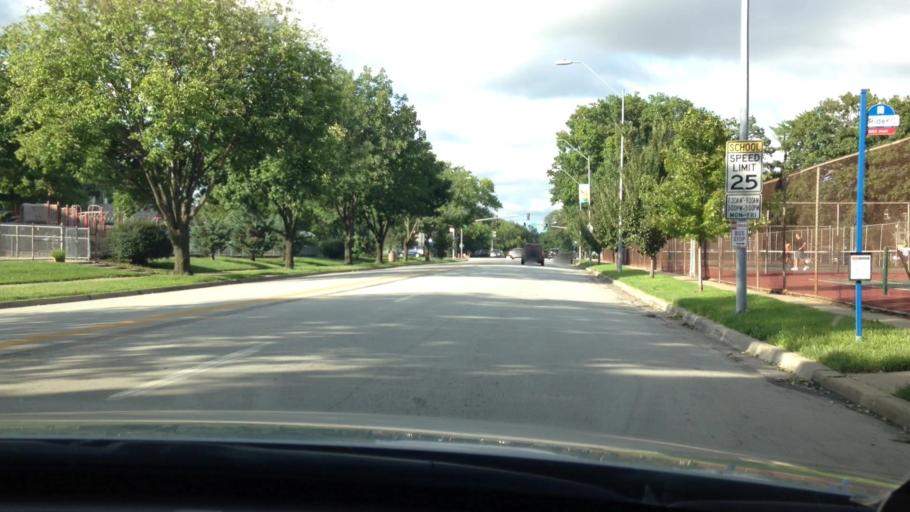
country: US
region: Kansas
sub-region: Johnson County
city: Mission Hills
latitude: 39.0127
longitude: -94.5921
